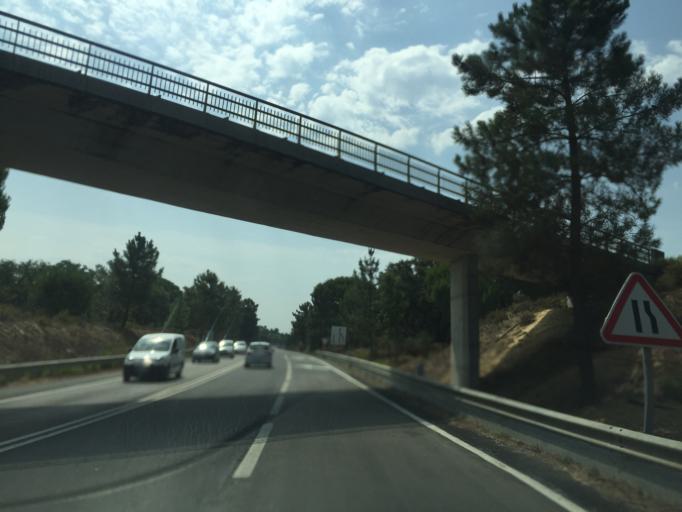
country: PT
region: Setubal
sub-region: Alcacer do Sal
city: Alcacer do Sal
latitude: 38.3529
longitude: -8.5211
